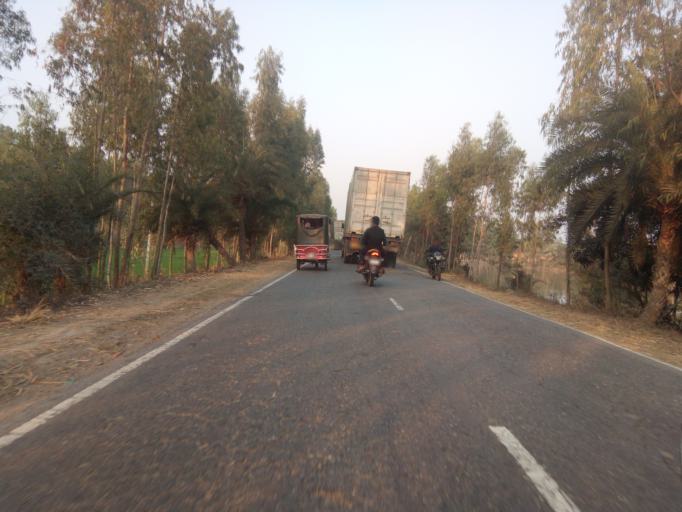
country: BD
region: Rajshahi
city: Par Naogaon
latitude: 24.5448
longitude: 89.1874
